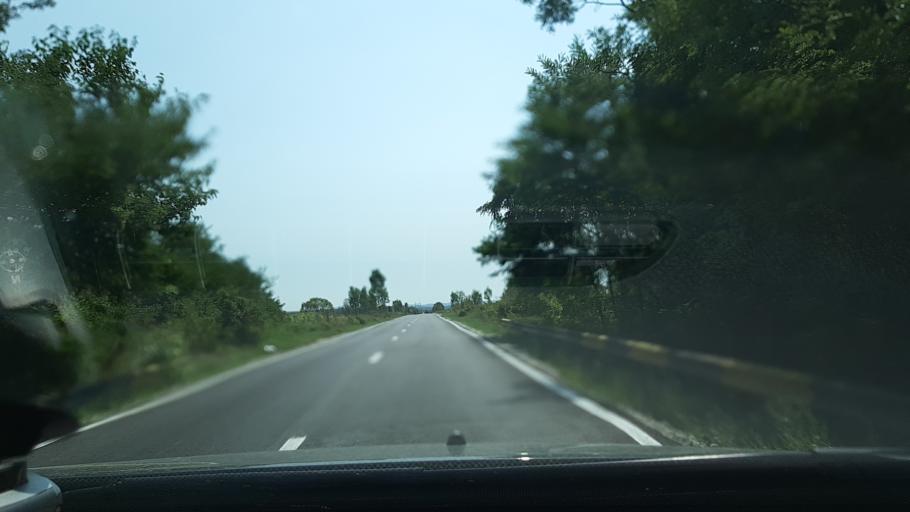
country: RO
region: Gorj
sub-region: Comuna Targu Carbunesti
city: Pojogeni
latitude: 45.0077
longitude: 23.4810
